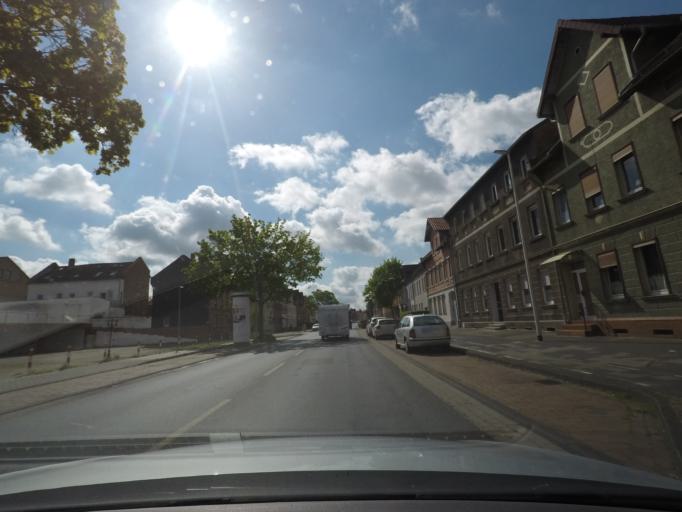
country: DE
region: Lower Saxony
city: Helmstedt
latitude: 52.2358
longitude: 11.0031
